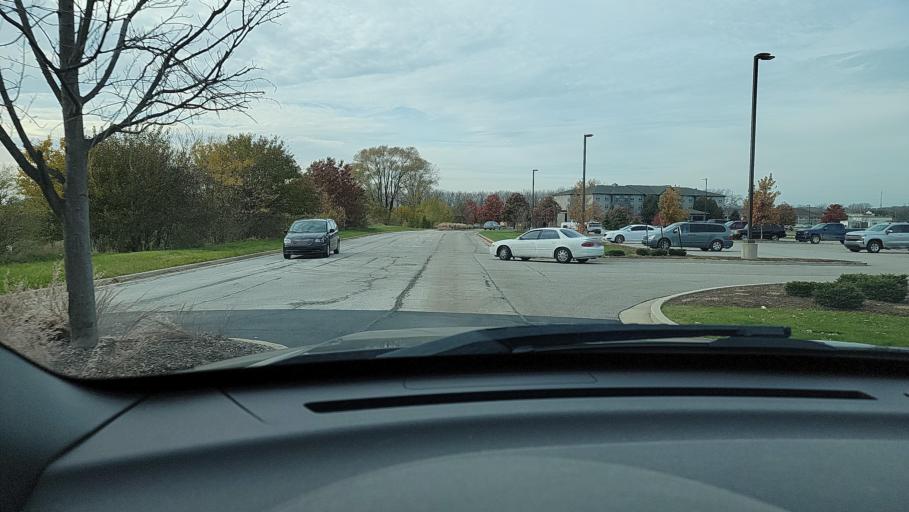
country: US
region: Indiana
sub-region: Porter County
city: Portage
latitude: 41.6033
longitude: -87.1703
